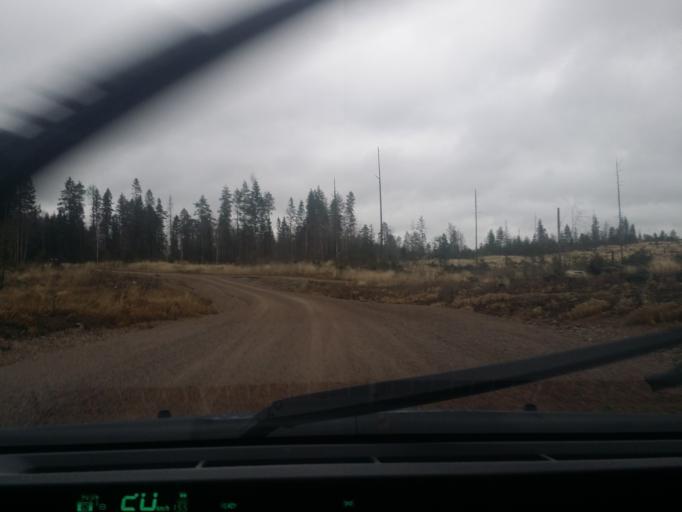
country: SE
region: Vaestmanland
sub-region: Norbergs Kommun
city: Norberg
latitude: 60.1082
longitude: 15.9807
